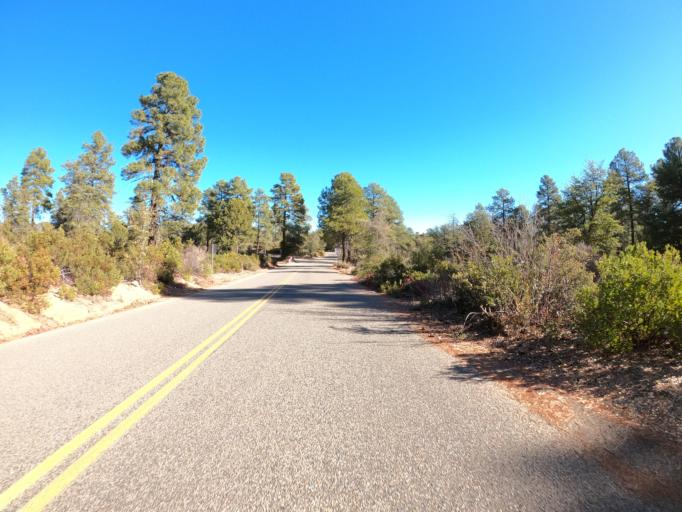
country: US
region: Arizona
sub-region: Yavapai County
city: Verde Village
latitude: 34.5853
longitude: -112.0585
